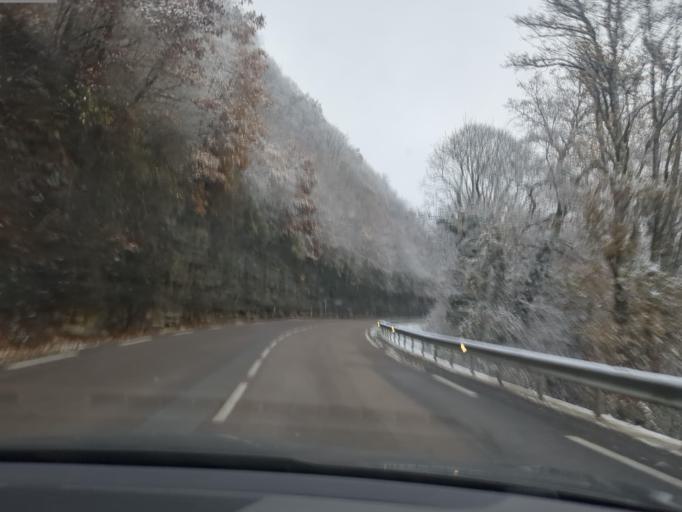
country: FR
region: Franche-Comte
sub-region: Departement du Jura
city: Perrigny
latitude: 46.6309
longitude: 5.6124
